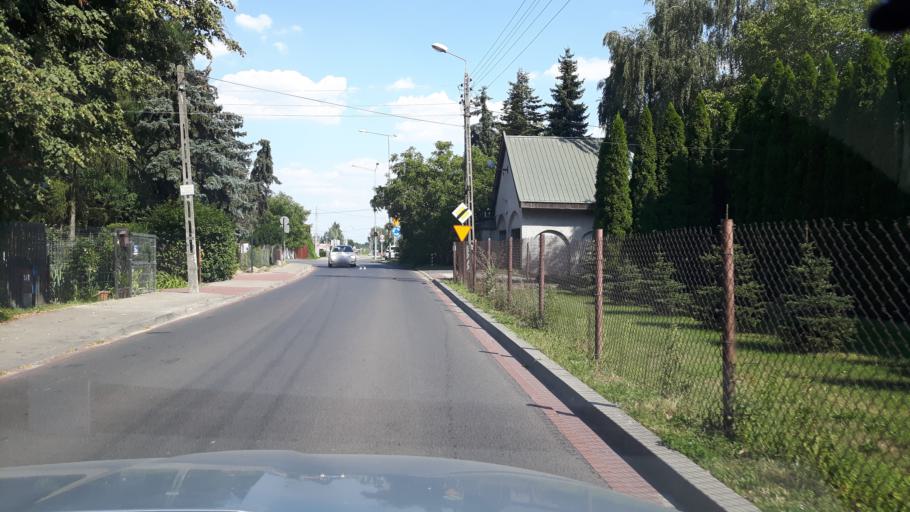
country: PL
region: Masovian Voivodeship
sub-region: Powiat pruszkowski
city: Nowe Grocholice
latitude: 52.1782
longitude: 20.9055
